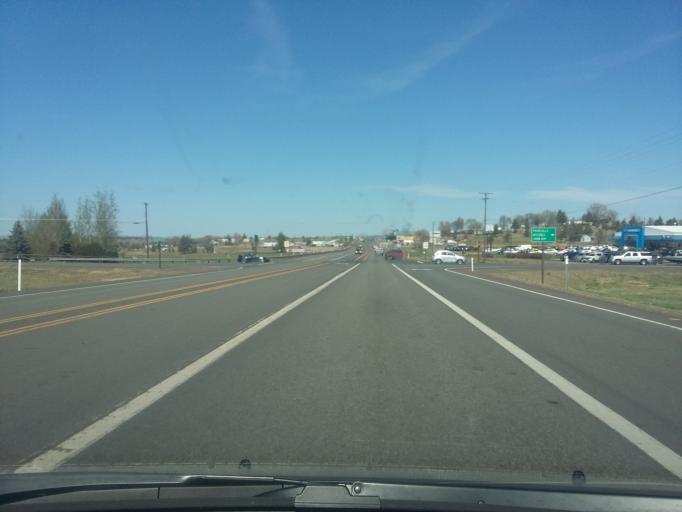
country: US
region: Oregon
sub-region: Jefferson County
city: Madras
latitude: 44.6061
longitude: -121.1395
